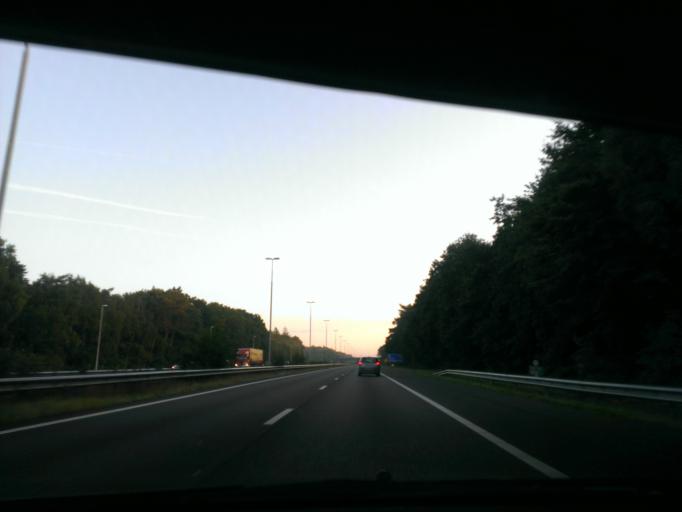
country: NL
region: Gelderland
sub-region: Gemeente Heerde
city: Heerde
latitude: 52.4062
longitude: 6.0154
